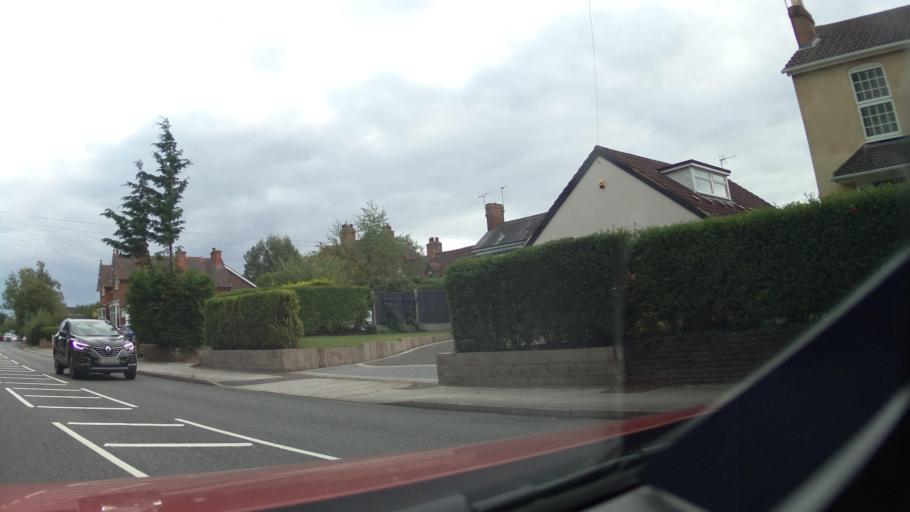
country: GB
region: England
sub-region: Solihull
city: Cheswick Green
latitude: 52.3549
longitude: -1.7779
